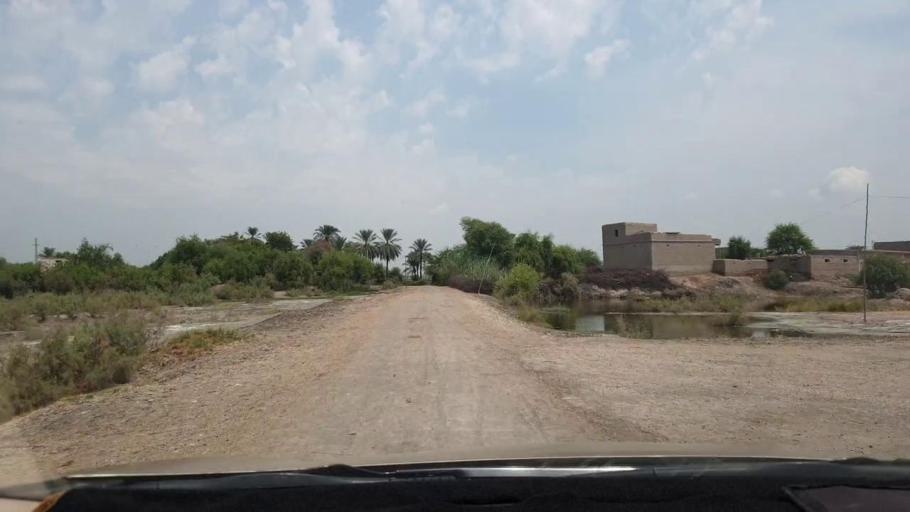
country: PK
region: Sindh
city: Naudero
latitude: 27.7283
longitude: 68.3527
